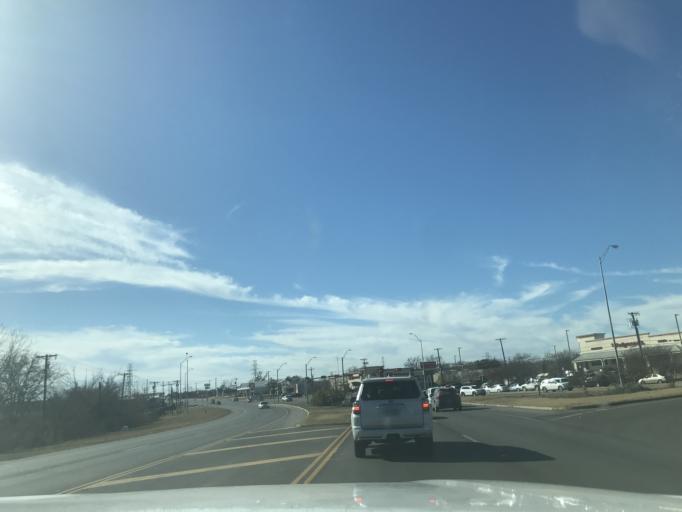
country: US
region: Texas
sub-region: Erath County
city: Stephenville
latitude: 32.2074
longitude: -98.2290
